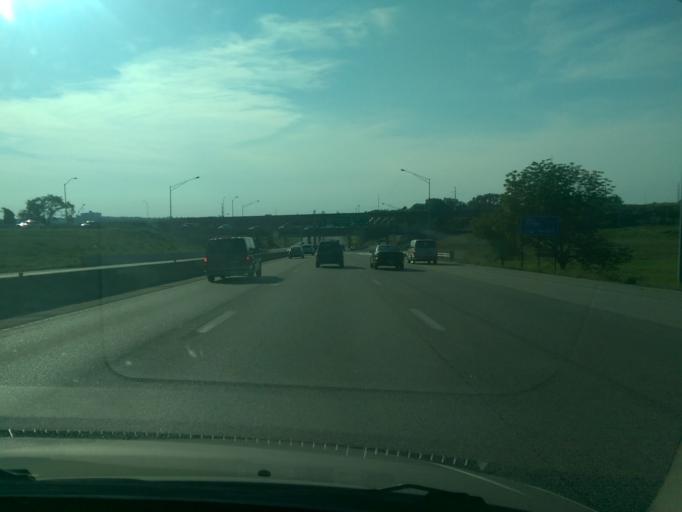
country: US
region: Missouri
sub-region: Jackson County
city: Raytown
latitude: 39.0576
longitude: -94.4866
